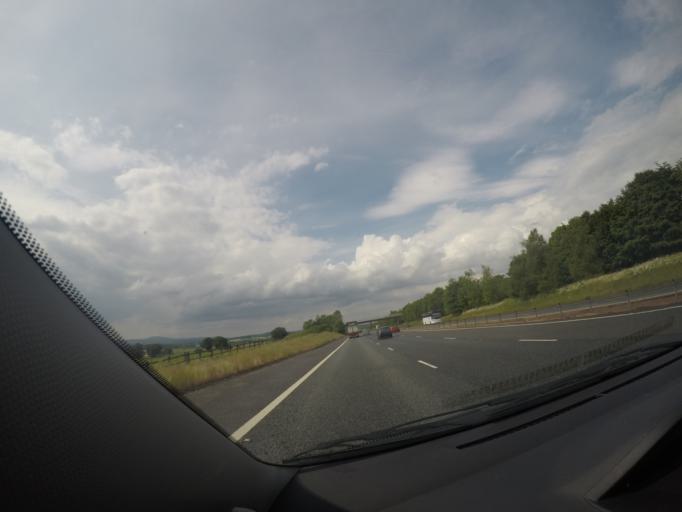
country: GB
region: Scotland
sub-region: Dumfries and Galloway
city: Lochmaben
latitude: 55.1806
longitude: -3.4053
